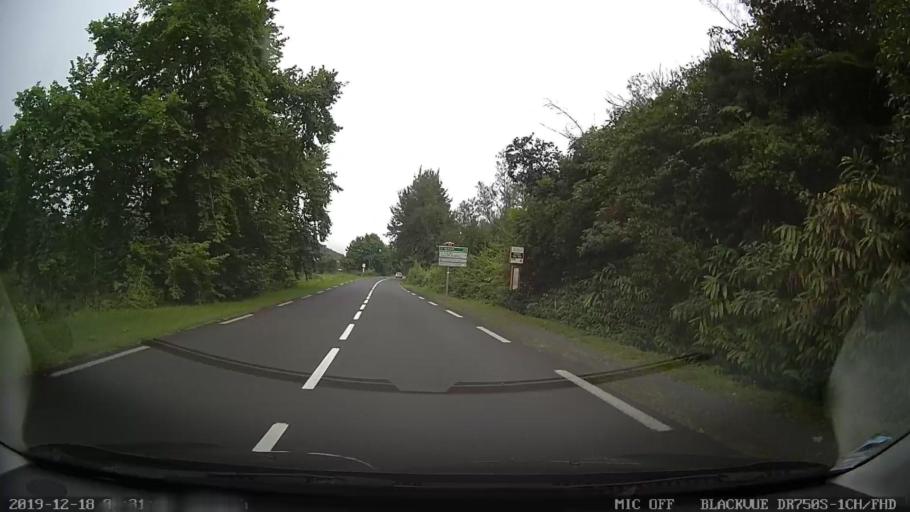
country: RE
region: Reunion
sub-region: Reunion
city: Cilaos
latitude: -21.1578
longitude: 55.6047
